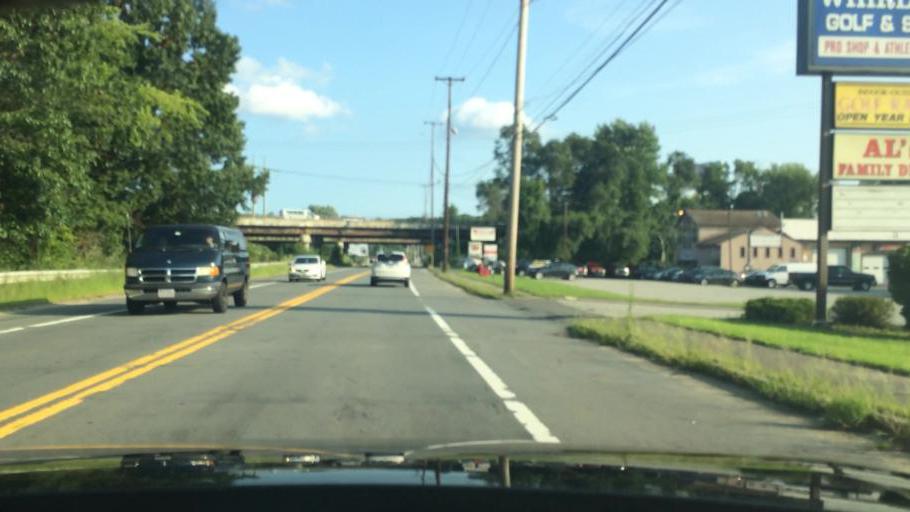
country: US
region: Massachusetts
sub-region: Essex County
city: North Andover
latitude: 42.7546
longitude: -71.1297
